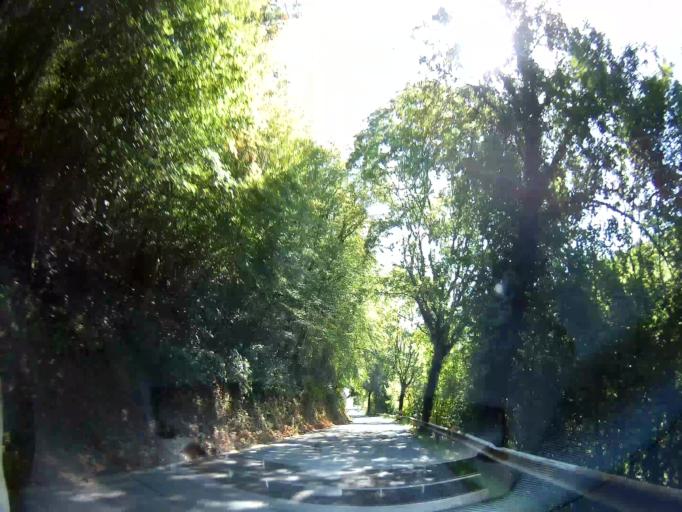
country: BE
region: Wallonia
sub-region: Province de Namur
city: Houyet
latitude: 50.2233
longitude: 4.9876
